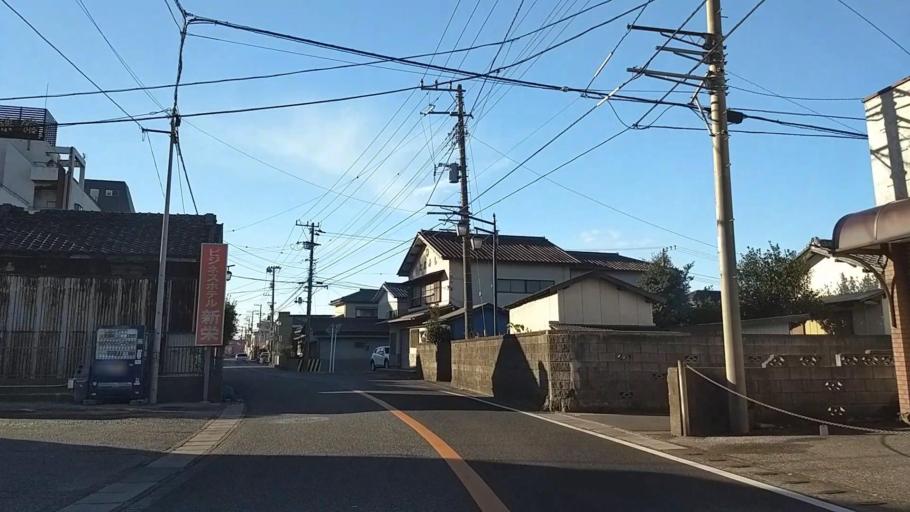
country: JP
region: Chiba
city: Kimitsu
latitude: 35.3381
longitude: 139.8641
